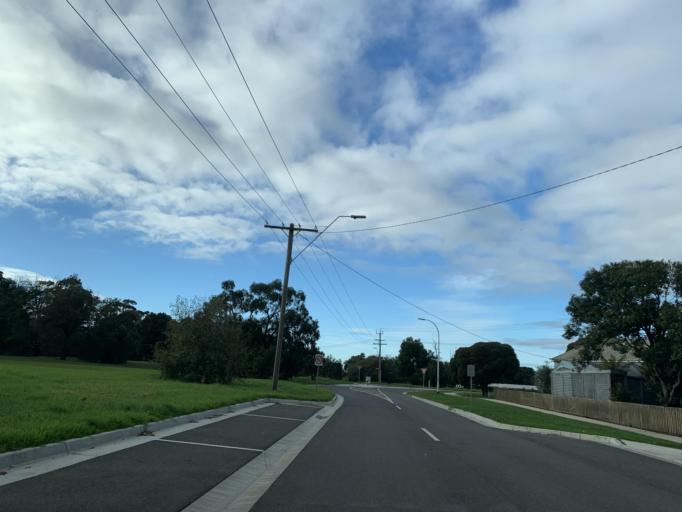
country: AU
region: Victoria
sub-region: Casey
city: Junction Village
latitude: -38.1338
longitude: 145.3316
